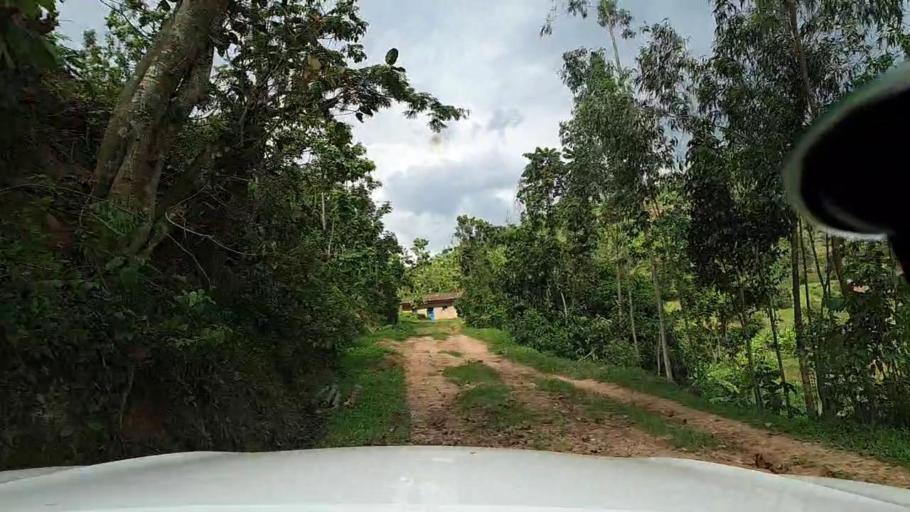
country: RW
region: Southern Province
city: Gitarama
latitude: -1.8201
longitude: 29.8009
